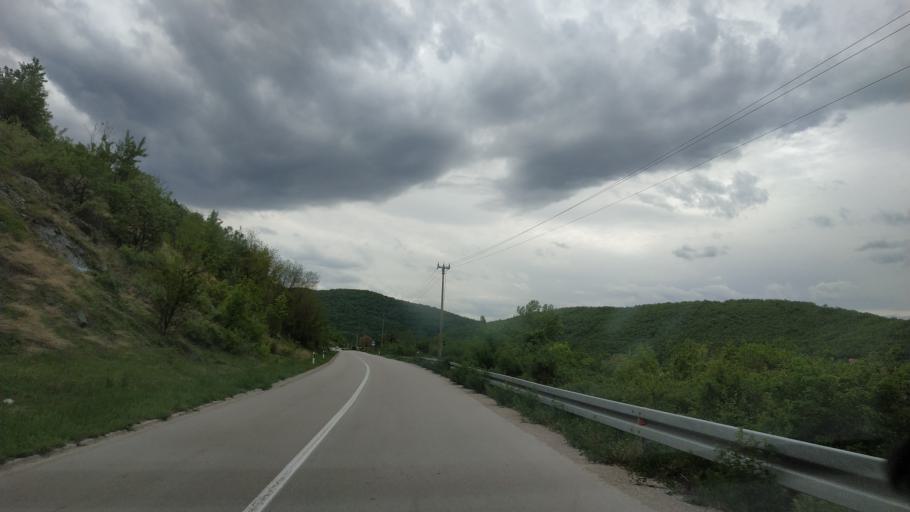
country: RS
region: Central Serbia
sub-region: Nisavski Okrug
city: Aleksinac
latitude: 43.6504
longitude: 21.7140
